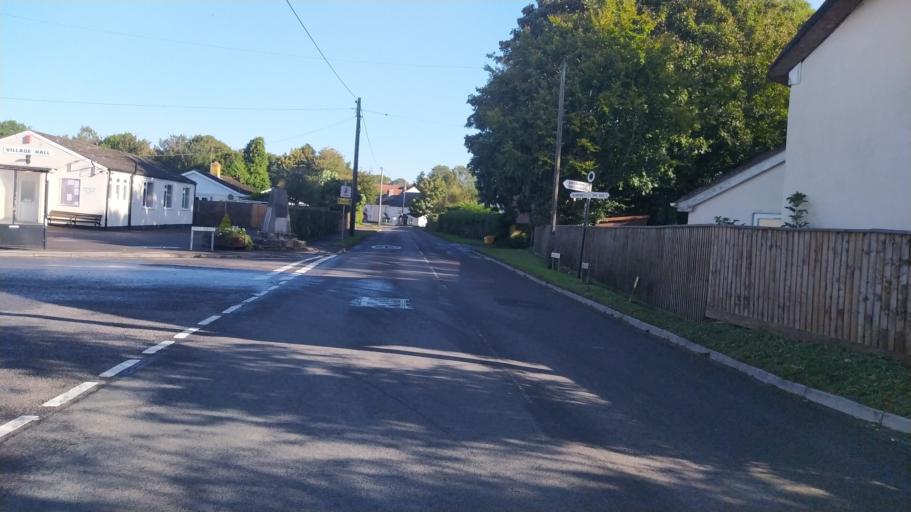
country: GB
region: England
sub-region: Dorset
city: Bovington Camp
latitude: 50.7783
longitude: -2.1975
